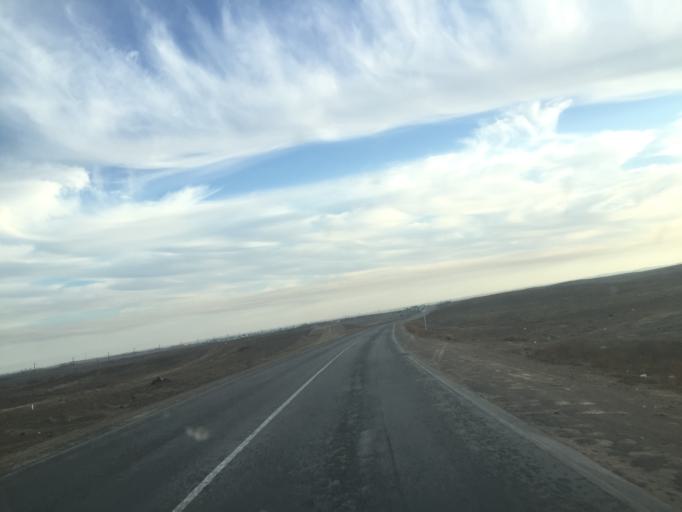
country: KZ
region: Almaty Oblysy
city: Ulken
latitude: 45.1358
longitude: 73.9649
